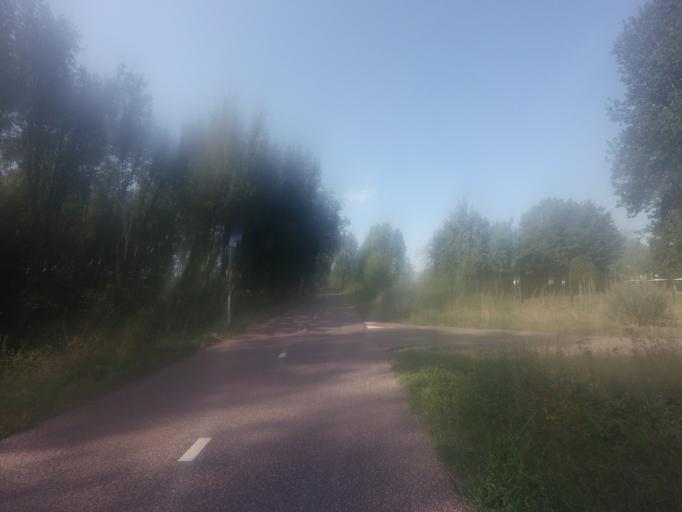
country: NL
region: North Brabant
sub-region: Gemeente Goirle
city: Goirle
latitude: 51.5412
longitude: 5.0328
